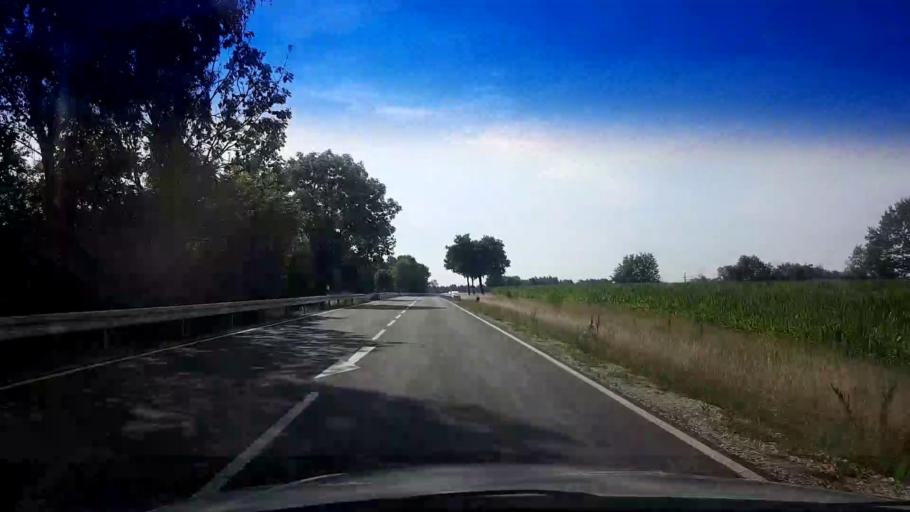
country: DE
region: Bavaria
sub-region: Upper Franconia
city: Mistelgau
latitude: 49.9446
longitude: 11.4472
